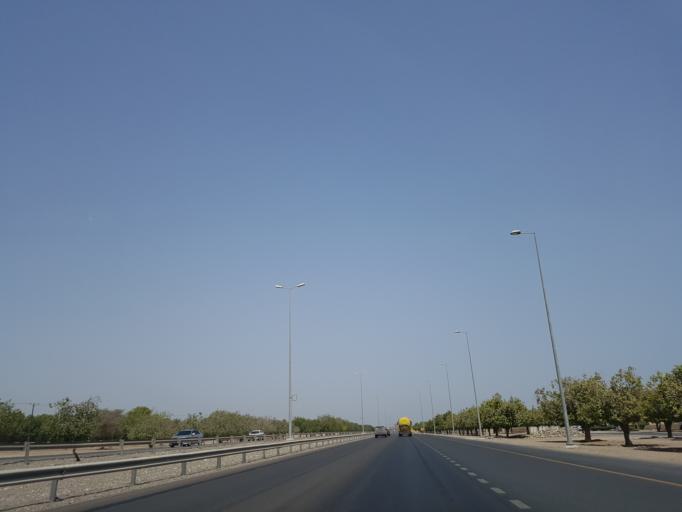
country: OM
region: Al Batinah
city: Saham
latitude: 24.1174
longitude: 56.9073
